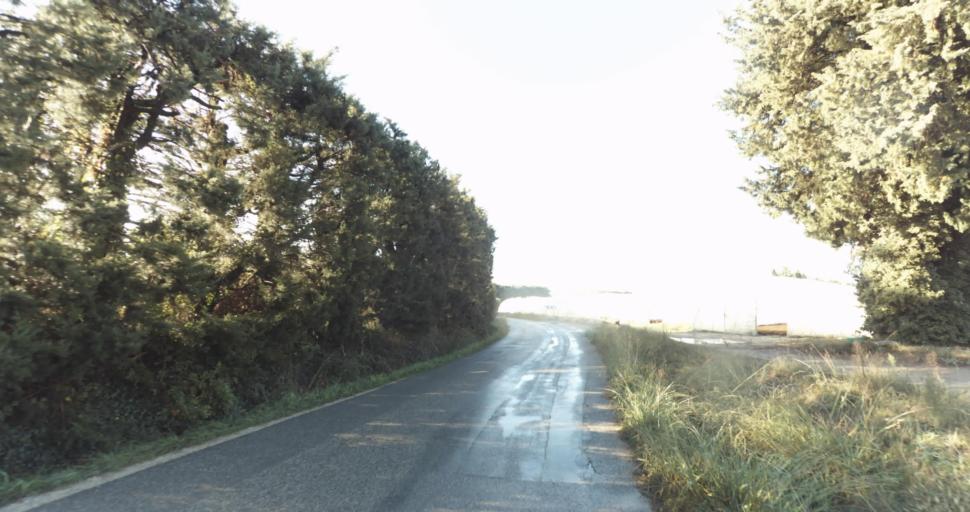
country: FR
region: Provence-Alpes-Cote d'Azur
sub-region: Departement des Bouches-du-Rhone
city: Rognonas
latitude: 43.8900
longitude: 4.7959
